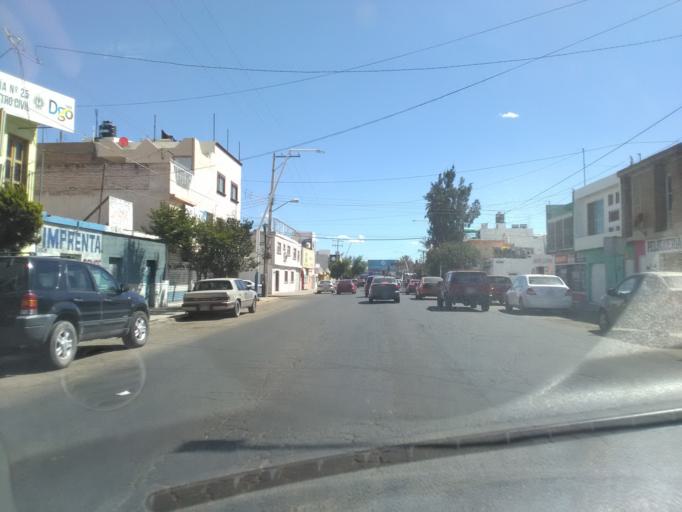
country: MX
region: Durango
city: Victoria de Durango
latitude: 24.0228
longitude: -104.6553
